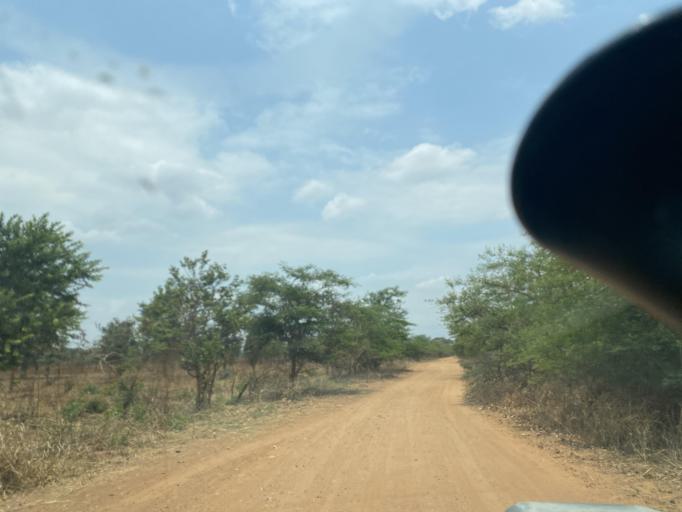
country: ZM
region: Lusaka
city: Chongwe
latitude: -15.5202
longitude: 28.8217
